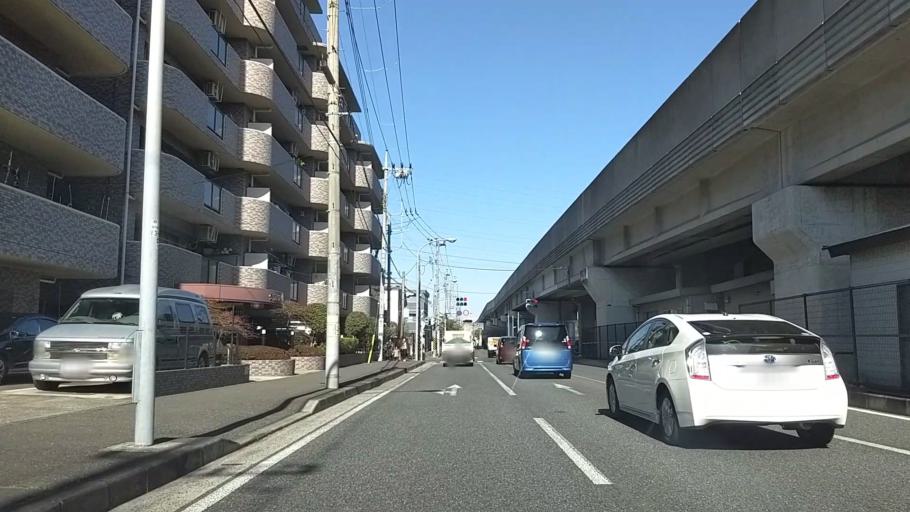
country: JP
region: Kanagawa
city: Yokohama
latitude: 35.5234
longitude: 139.6123
